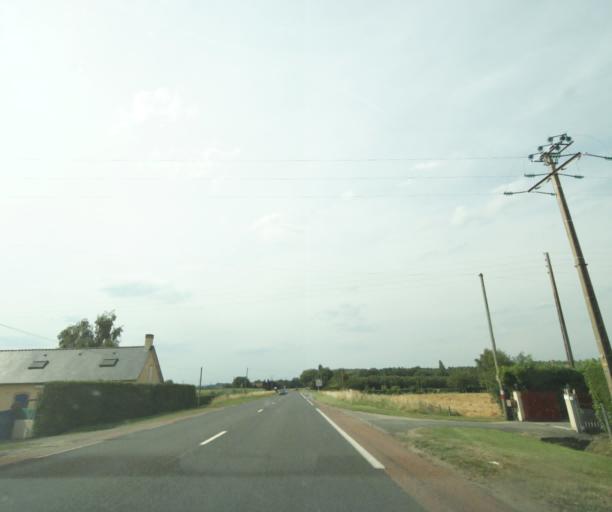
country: FR
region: Pays de la Loire
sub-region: Departement de la Sarthe
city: Ecommoy
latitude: 47.8506
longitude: 0.2547
